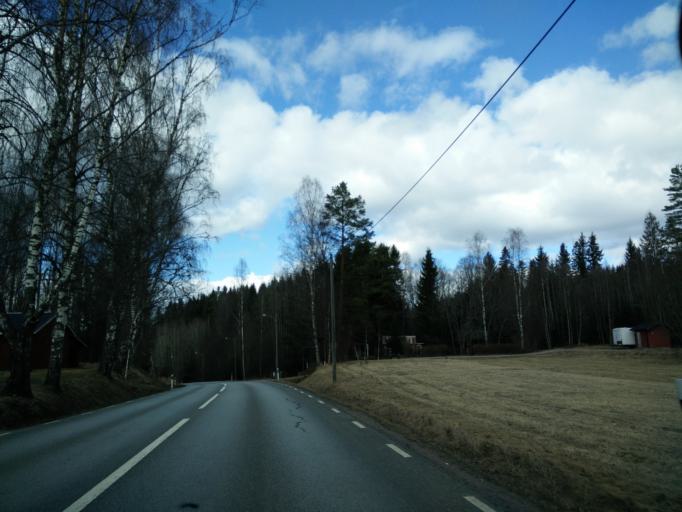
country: SE
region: Vaermland
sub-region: Munkfors Kommun
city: Munkfors
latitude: 59.8893
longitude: 13.5645
